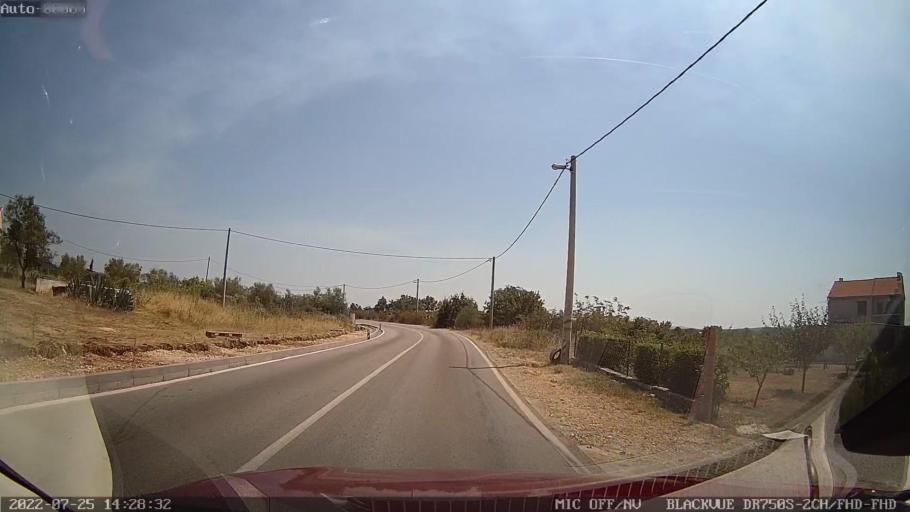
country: HR
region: Zadarska
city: Policnik
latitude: 44.1253
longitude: 15.3490
